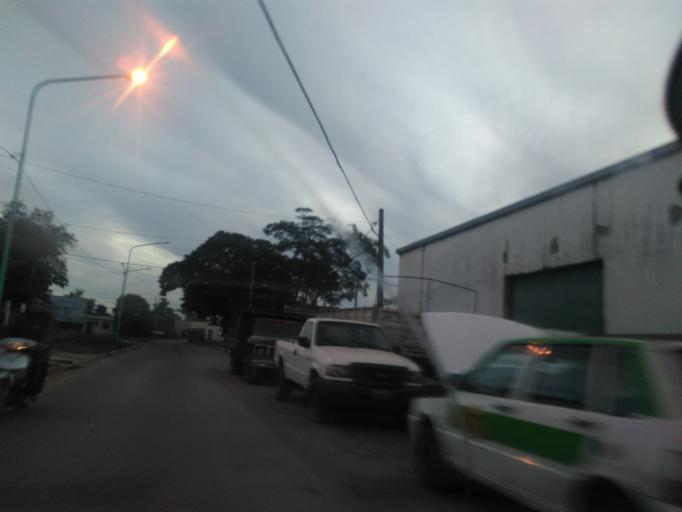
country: AR
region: Chaco
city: Resistencia
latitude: -27.4332
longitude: -58.9969
